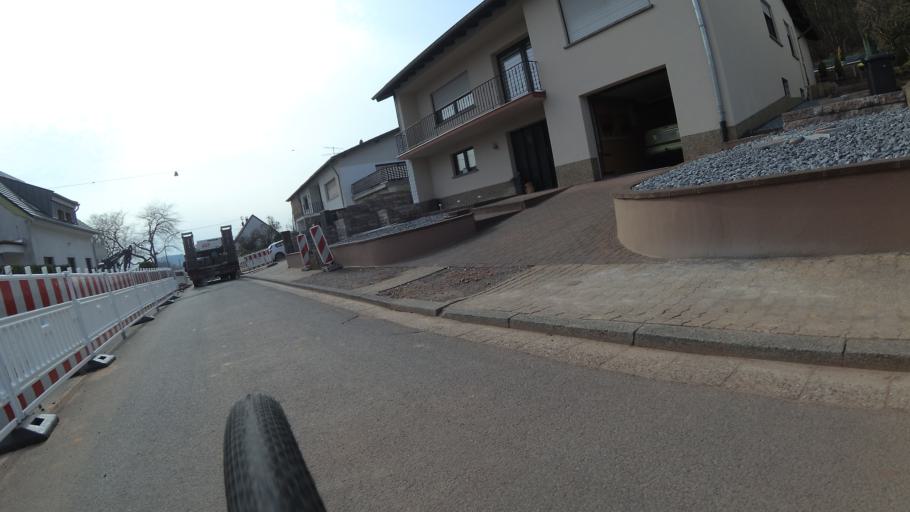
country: DE
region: Saarland
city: Losheim
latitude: 49.4533
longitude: 6.7636
